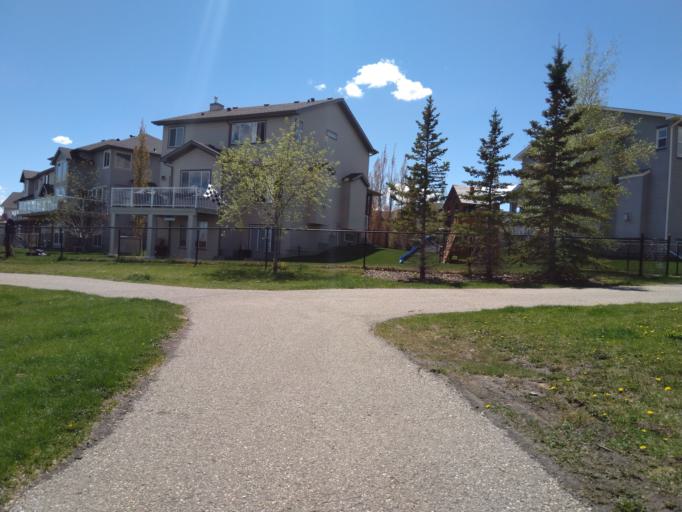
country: CA
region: Alberta
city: Chestermere
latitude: 51.0338
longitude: -113.8391
